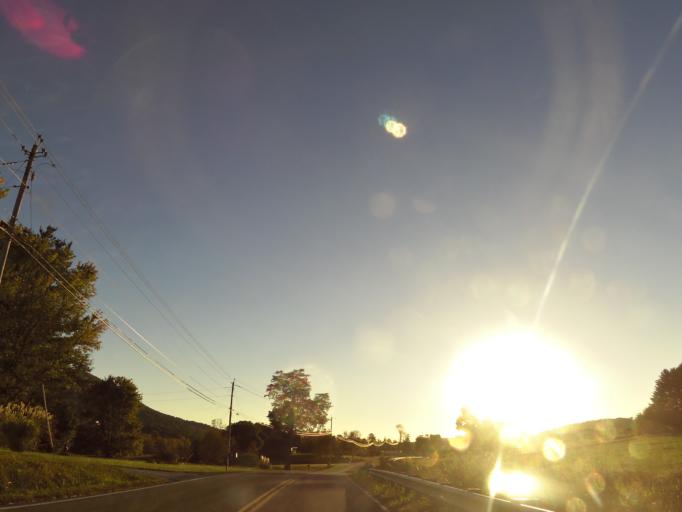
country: US
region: Tennessee
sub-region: Grainger County
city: Rutledge
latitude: 36.2823
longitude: -83.6152
